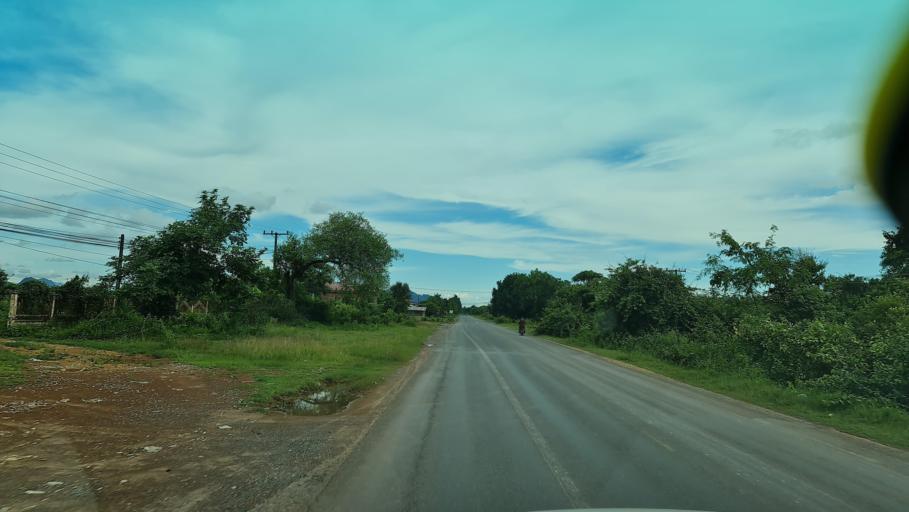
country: TH
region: Nakhon Phanom
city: Ban Phaeng
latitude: 18.0886
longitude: 104.2896
